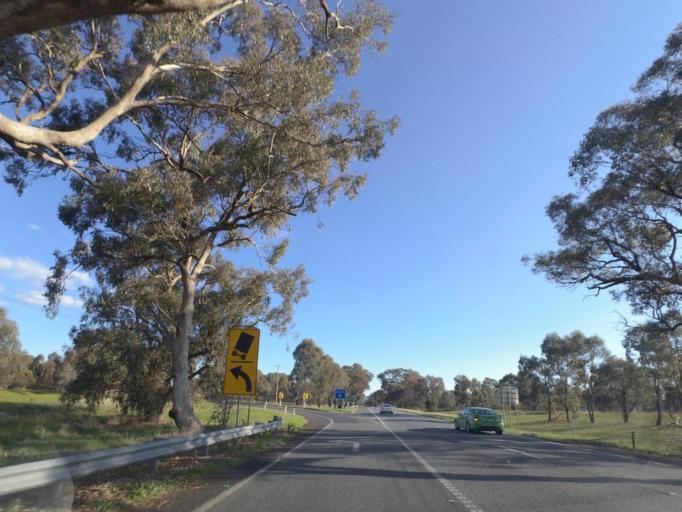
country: AU
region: Victoria
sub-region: Benalla
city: Benalla
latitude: -36.6938
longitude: 145.6596
